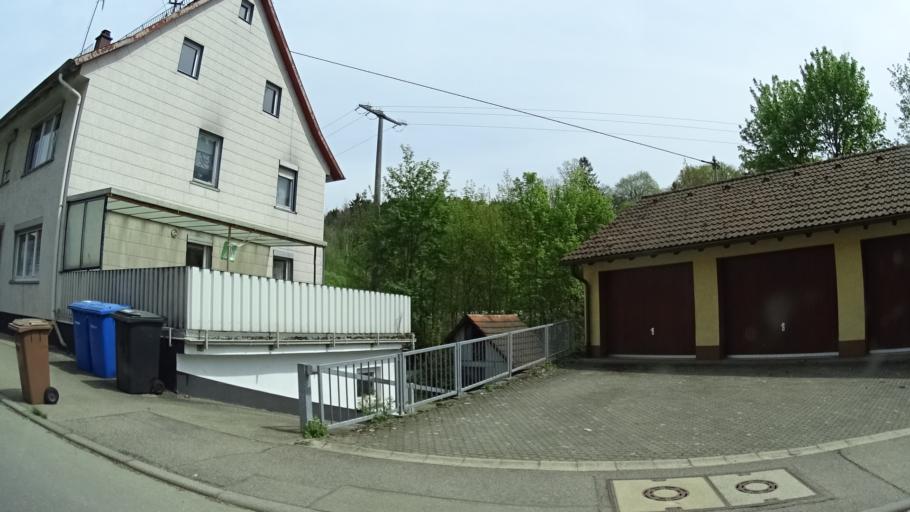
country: DE
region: Baden-Wuerttemberg
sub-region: Freiburg Region
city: Rottweil
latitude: 48.1397
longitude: 8.6266
